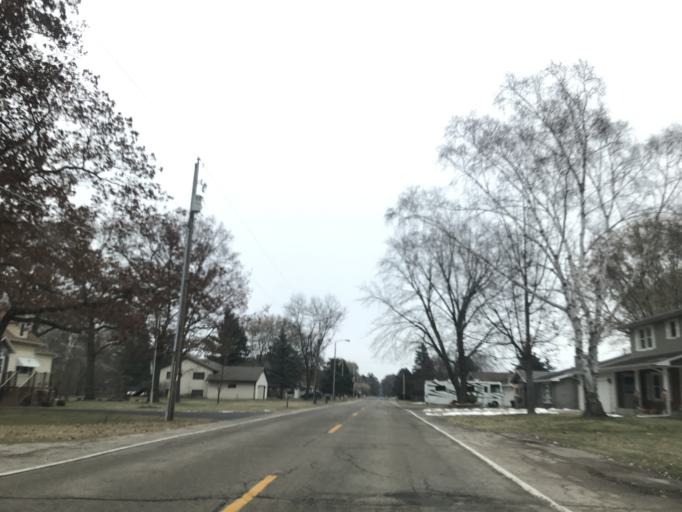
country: US
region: Wisconsin
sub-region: Marinette County
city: Marinette
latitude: 45.0781
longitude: -87.6217
